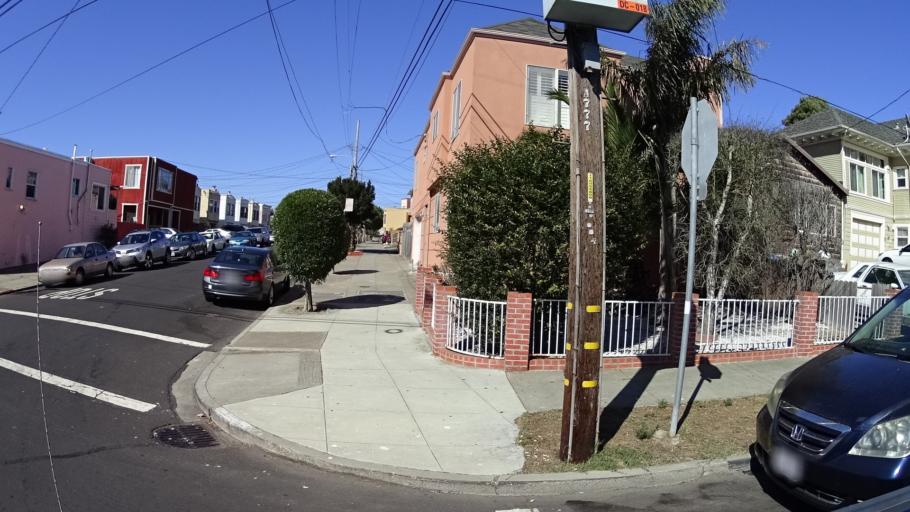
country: US
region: California
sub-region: San Mateo County
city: Daly City
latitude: 37.7016
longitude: -122.4675
